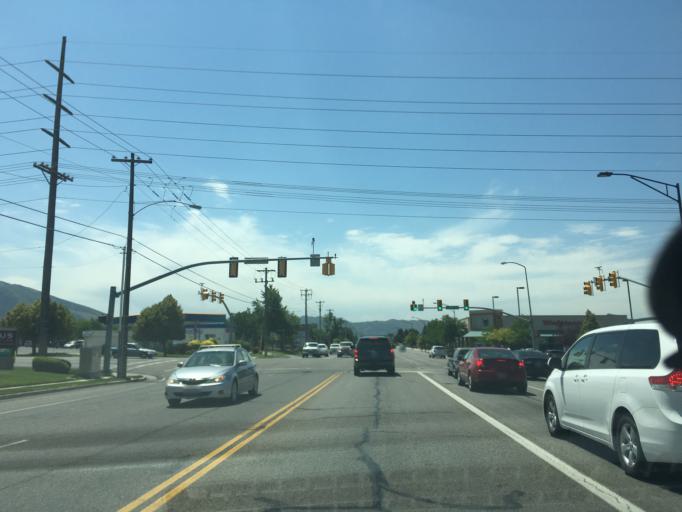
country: US
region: Utah
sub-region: Salt Lake County
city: Sandy City
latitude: 40.5811
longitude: -111.8722
